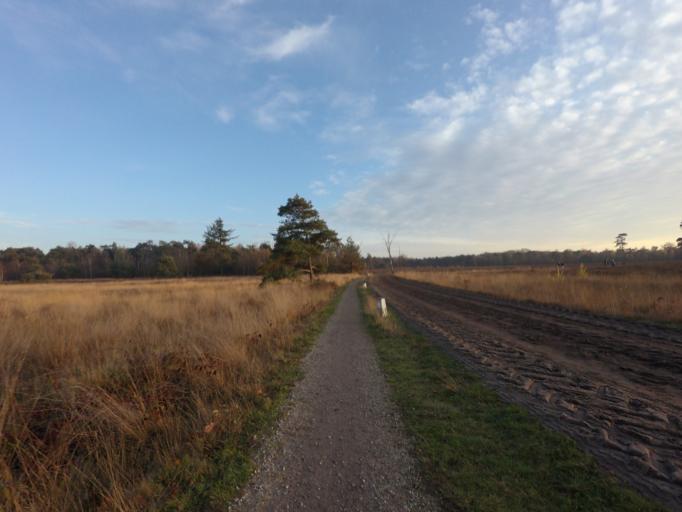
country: NL
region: North Brabant
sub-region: Gemeente Breda
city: Breda
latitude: 51.5061
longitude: 4.8180
